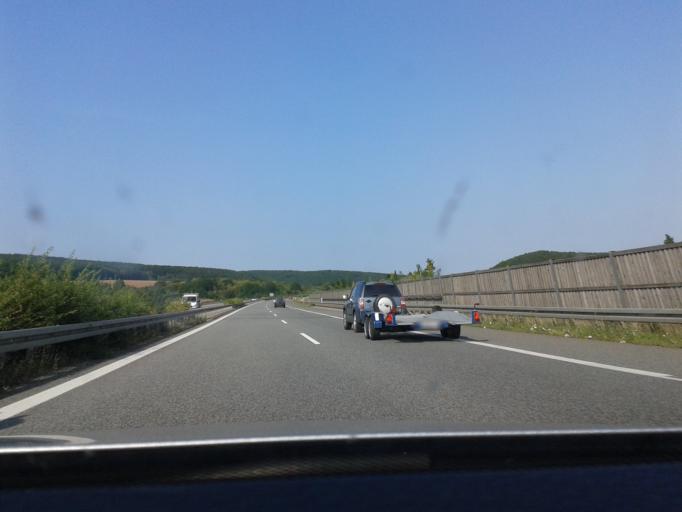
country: DE
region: Saxony-Anhalt
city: Rossla
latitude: 51.4698
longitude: 11.0492
